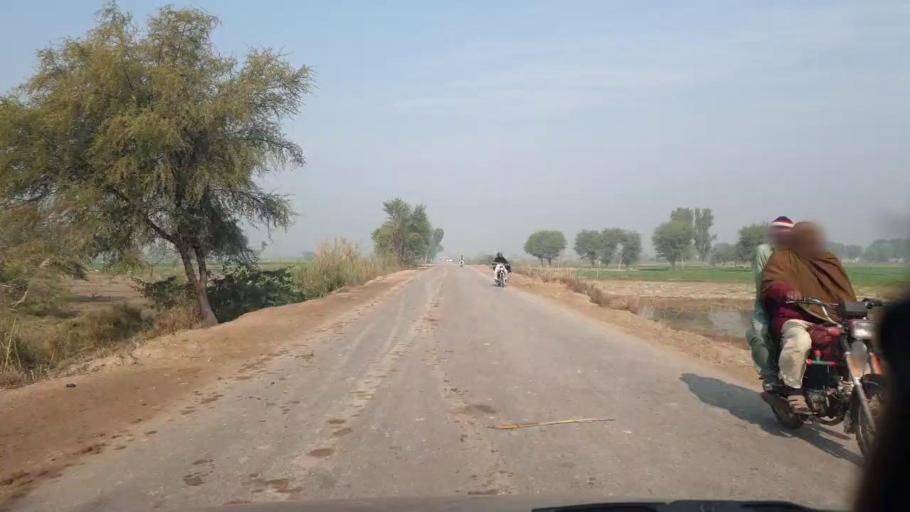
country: PK
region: Sindh
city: Shahdadpur
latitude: 25.9403
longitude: 68.6024
